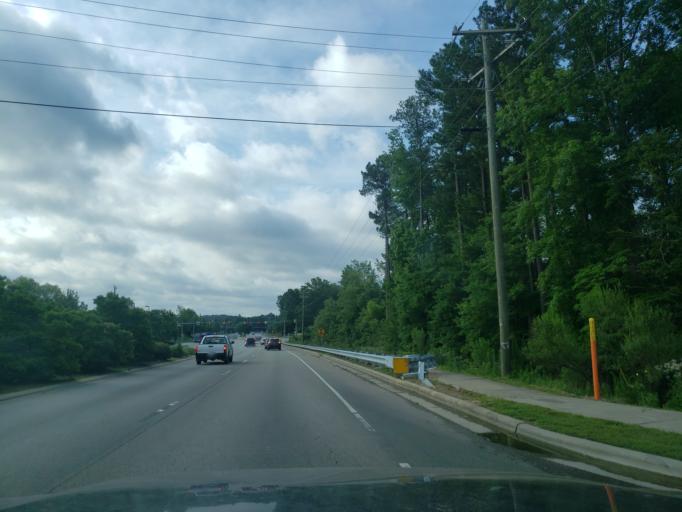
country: US
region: North Carolina
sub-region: Durham County
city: Durham
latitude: 35.9492
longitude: -78.9254
